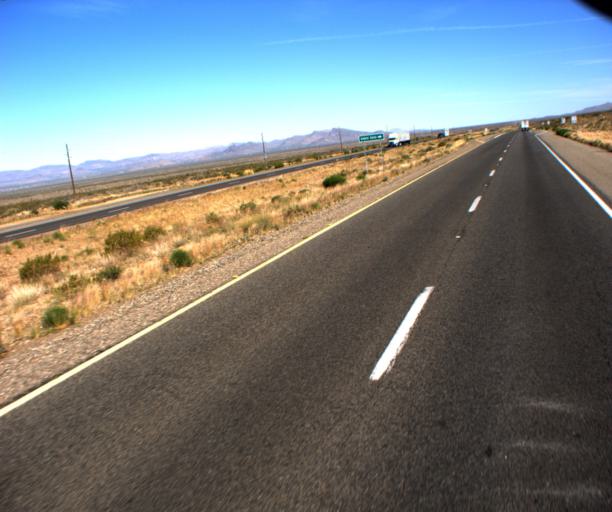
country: US
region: Arizona
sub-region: Mohave County
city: Golden Valley
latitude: 35.2494
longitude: -114.1523
